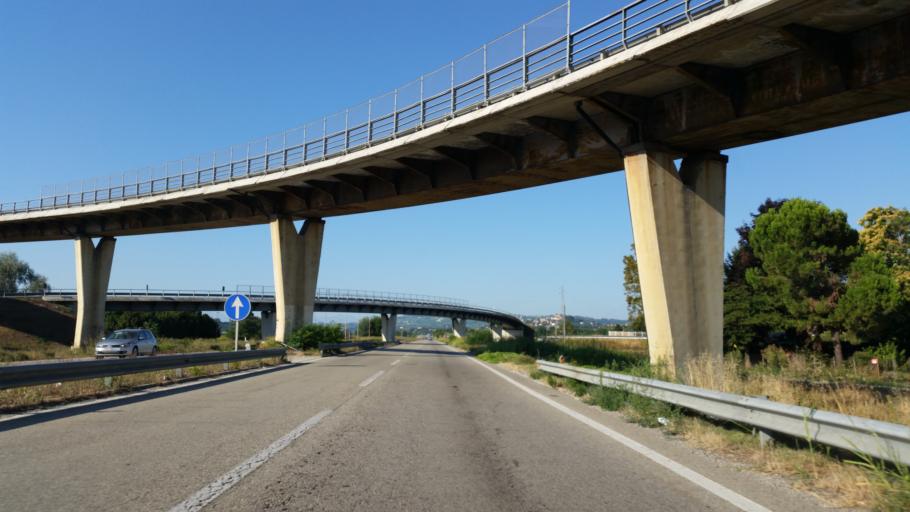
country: IT
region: Piedmont
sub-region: Provincia di Cuneo
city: Alba
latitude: 44.6988
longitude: 8.0095
